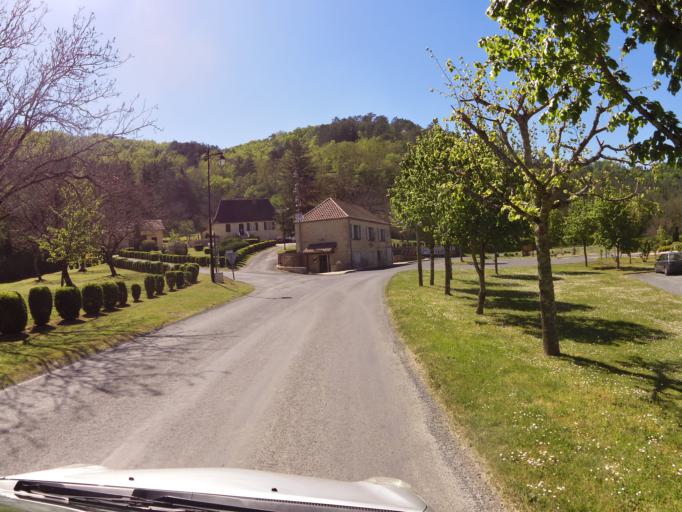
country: FR
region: Aquitaine
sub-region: Departement de la Dordogne
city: Cenac-et-Saint-Julien
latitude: 44.7874
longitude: 1.1677
